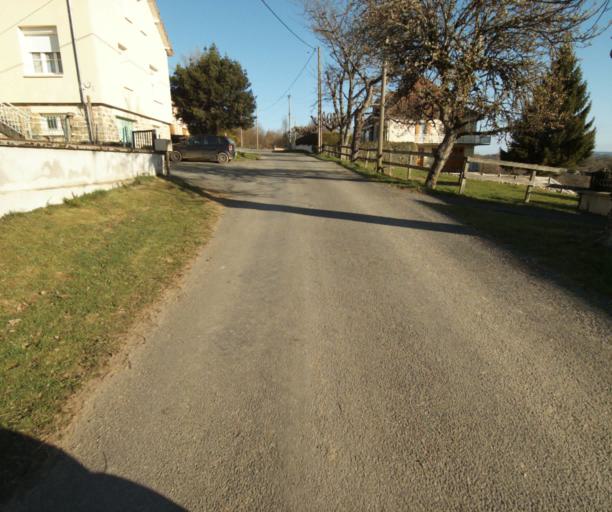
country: FR
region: Limousin
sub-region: Departement de la Correze
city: Seilhac
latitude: 45.3618
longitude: 1.7482
